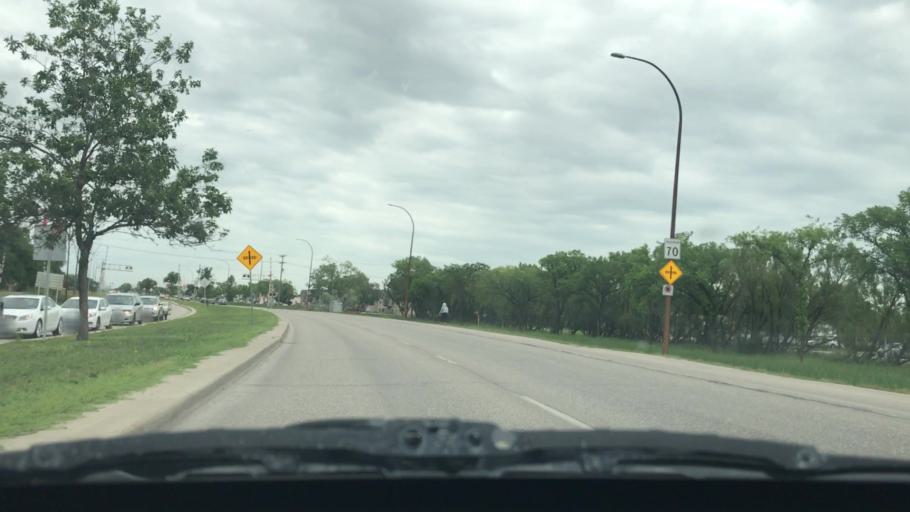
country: CA
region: Manitoba
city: Winnipeg
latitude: 49.8561
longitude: -97.0867
